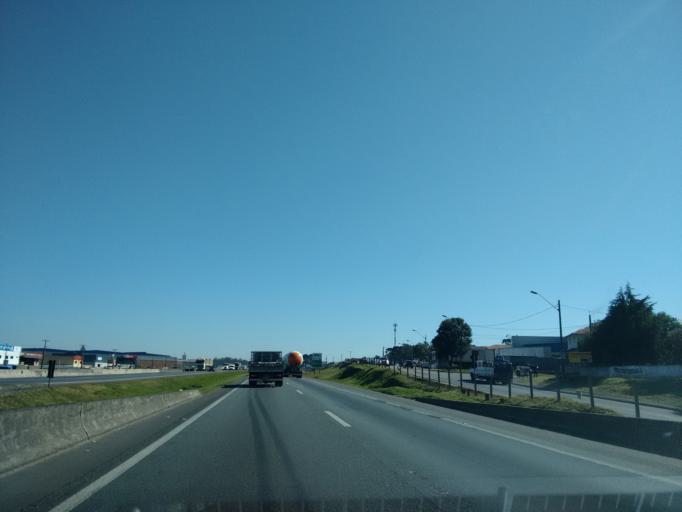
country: BR
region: Parana
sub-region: Sao Jose Dos Pinhais
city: Sao Jose dos Pinhais
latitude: -25.5534
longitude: -49.2764
